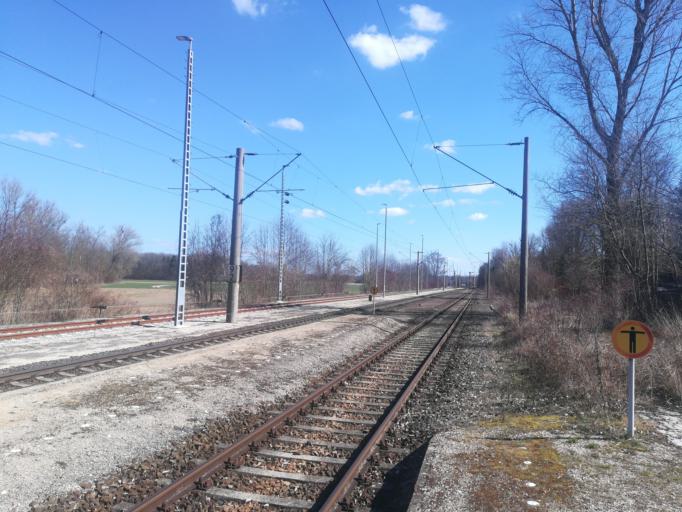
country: DE
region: Bavaria
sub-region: Upper Bavaria
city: Weichering
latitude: 48.7206
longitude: 11.3310
